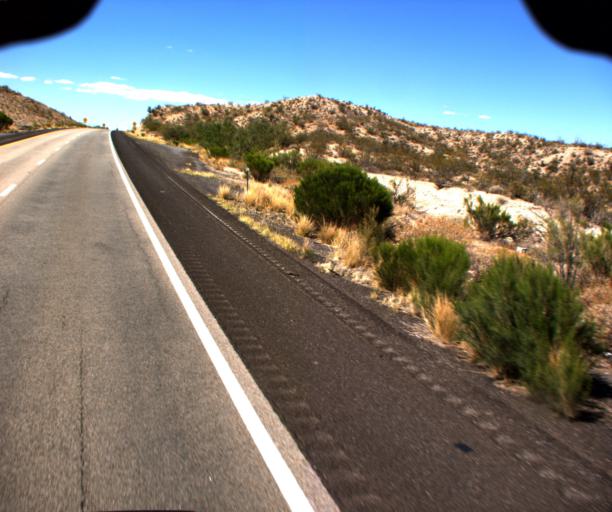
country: US
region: Arizona
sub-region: Mohave County
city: Kingman
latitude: 34.9019
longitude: -113.6553
